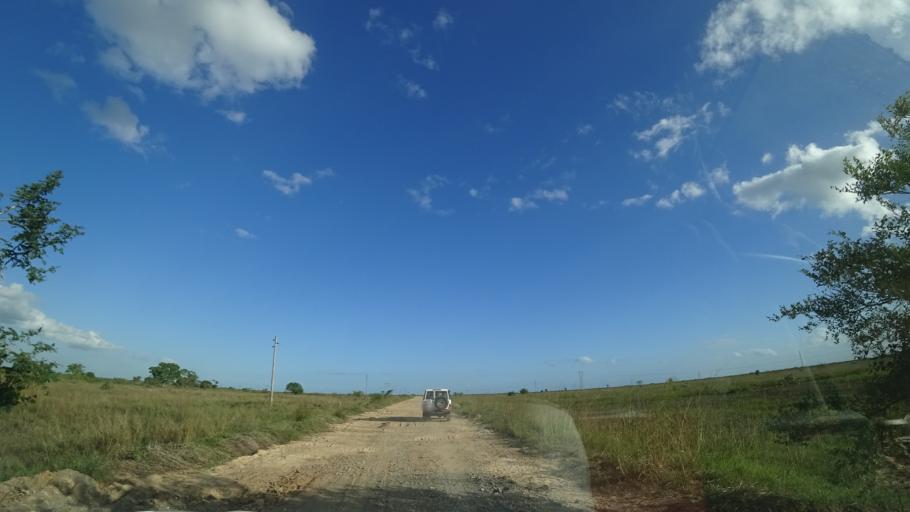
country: MZ
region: Sofala
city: Dondo
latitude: -19.4530
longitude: 34.5627
